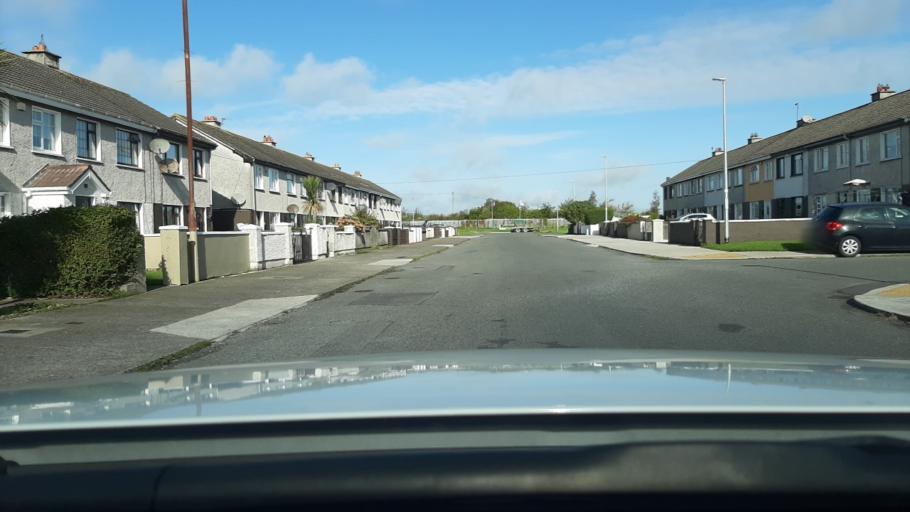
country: IE
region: Leinster
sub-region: Kildare
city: Kildare
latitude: 53.1619
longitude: -6.9051
